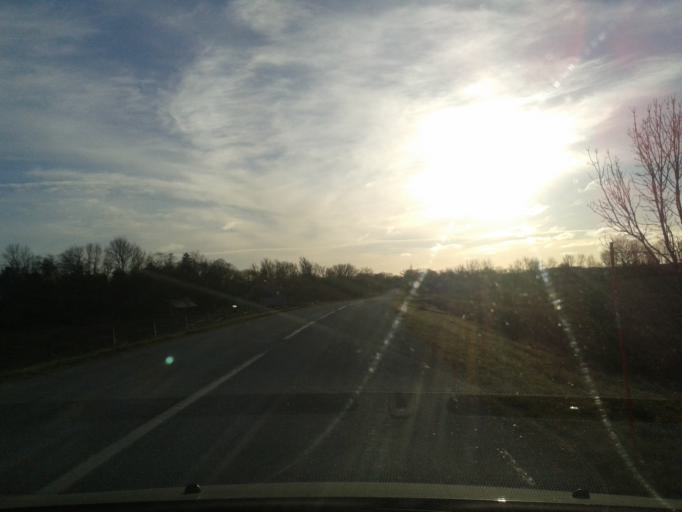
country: SE
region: Gotland
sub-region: Gotland
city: Hemse
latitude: 57.4266
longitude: 18.6324
